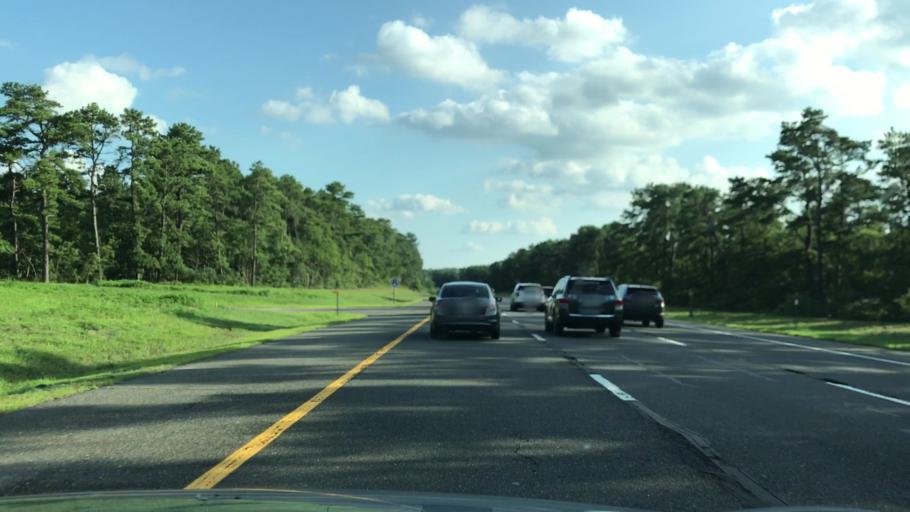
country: US
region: New Jersey
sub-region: Ocean County
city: Waretown
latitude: 39.8081
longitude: -74.2329
